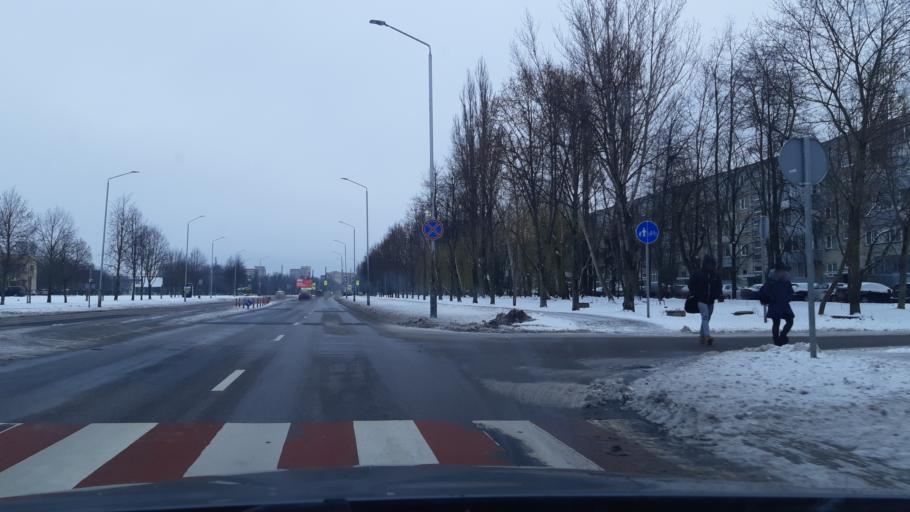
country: LT
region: Kauno apskritis
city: Dainava (Kaunas)
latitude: 54.9250
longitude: 23.9765
